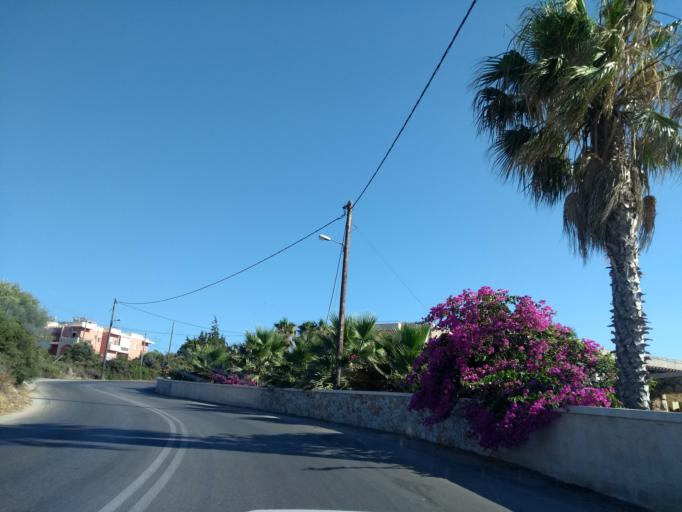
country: GR
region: Crete
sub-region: Nomos Chanias
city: Pithari
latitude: 35.5509
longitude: 24.0843
